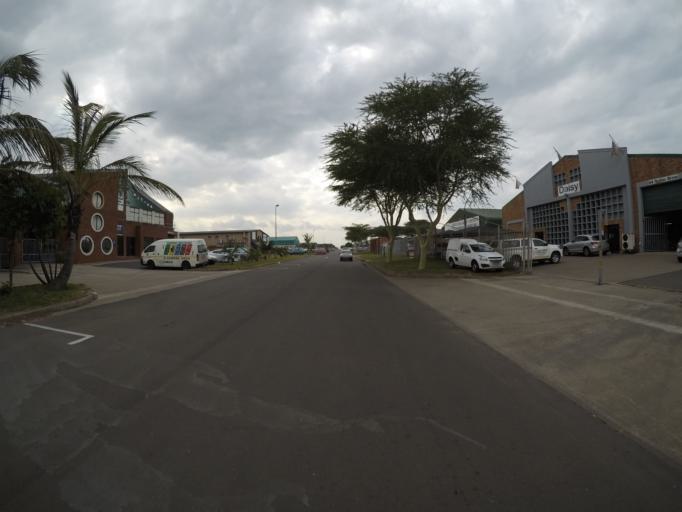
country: ZA
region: KwaZulu-Natal
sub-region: uThungulu District Municipality
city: Richards Bay
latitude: -28.7594
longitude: 32.0417
